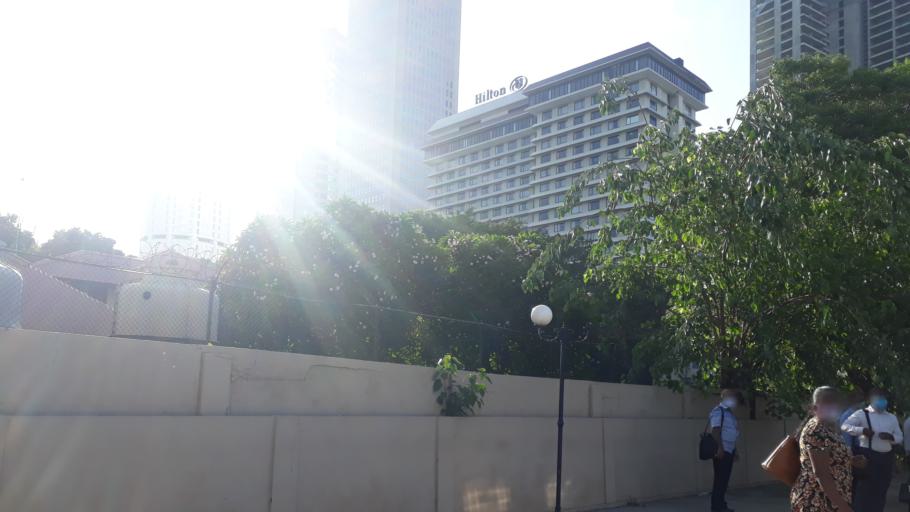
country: LK
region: Western
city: Colombo
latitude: 6.9310
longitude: 79.8460
